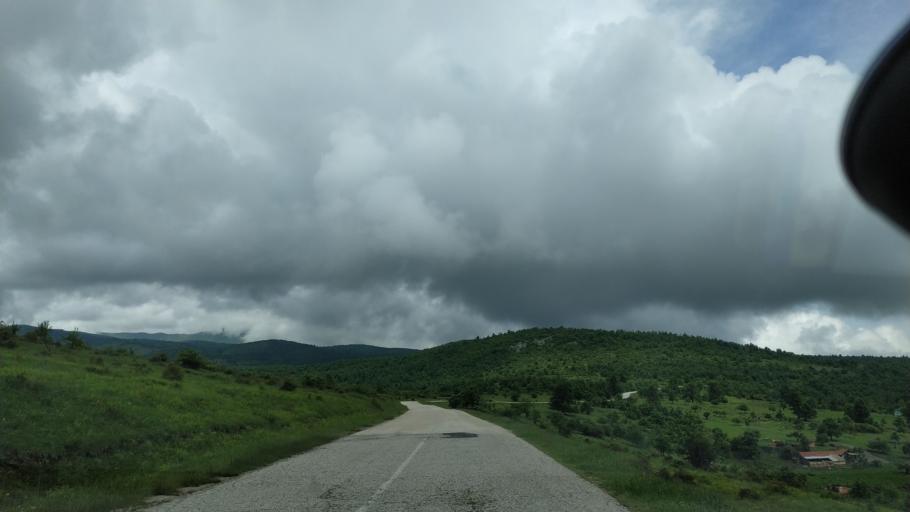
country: RS
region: Central Serbia
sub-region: Zajecarski Okrug
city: Soko Banja
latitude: 43.7103
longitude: 21.9403
